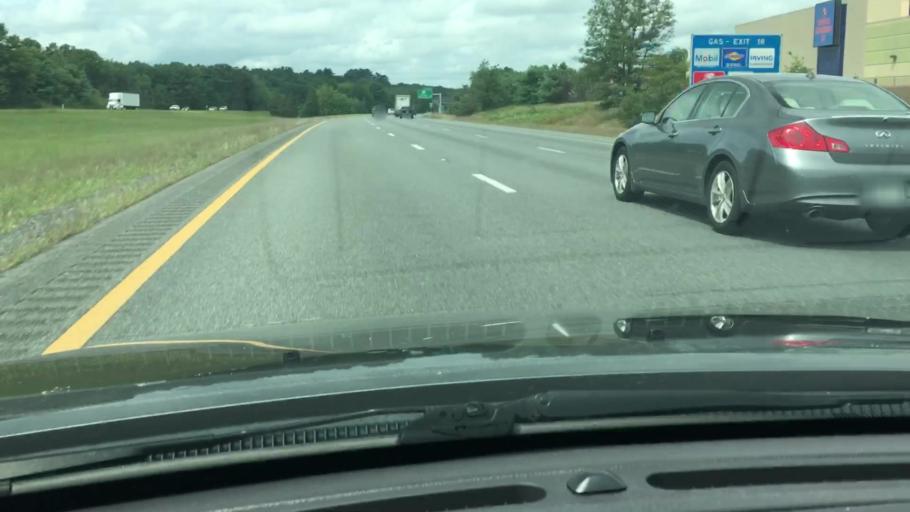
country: US
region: Massachusetts
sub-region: Norfolk County
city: Bellingham
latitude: 42.1092
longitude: -71.4603
